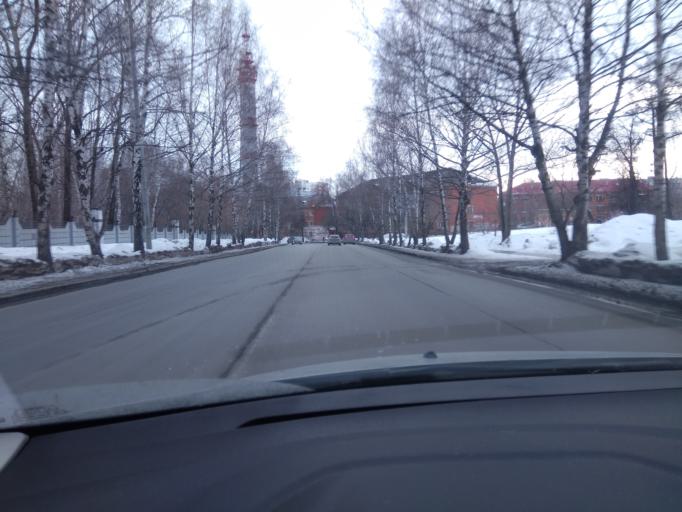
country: RU
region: Sverdlovsk
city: Yekaterinburg
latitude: 56.8495
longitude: 60.6372
